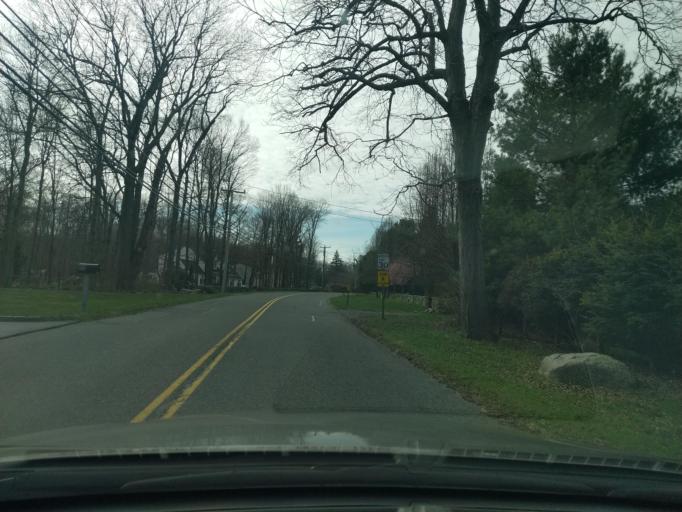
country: US
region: Connecticut
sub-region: Fairfield County
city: Trumbull
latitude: 41.3344
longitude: -73.2234
